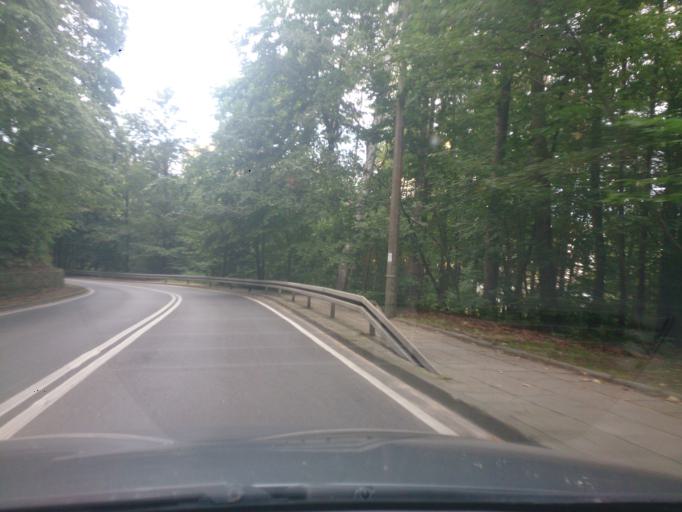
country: PL
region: Pomeranian Voivodeship
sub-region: Sopot
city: Sopot
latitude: 54.4555
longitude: 18.5366
